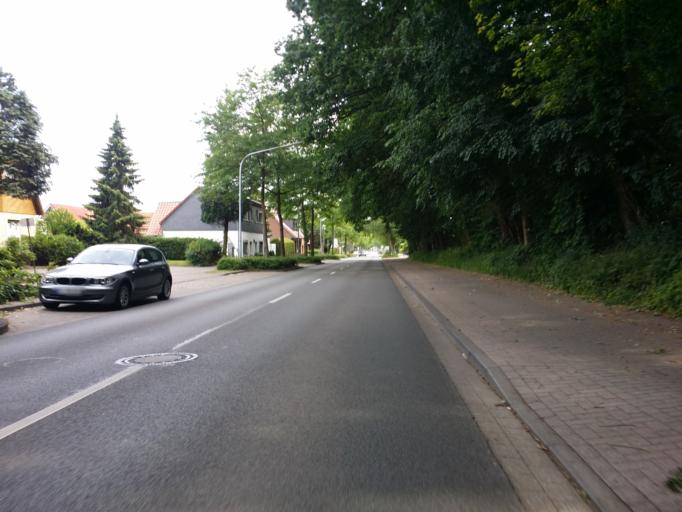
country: DE
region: Lower Saxony
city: Oldenburg
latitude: 53.1739
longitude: 8.2079
